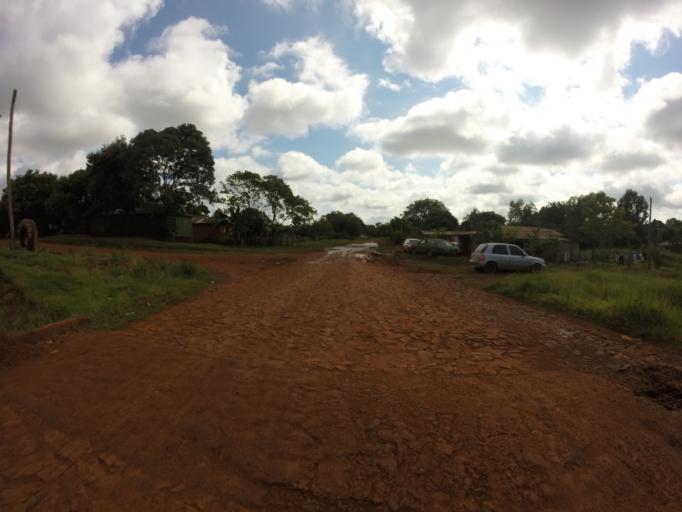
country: PY
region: Alto Parana
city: Ciudad del Este
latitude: -25.4041
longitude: -54.6535
